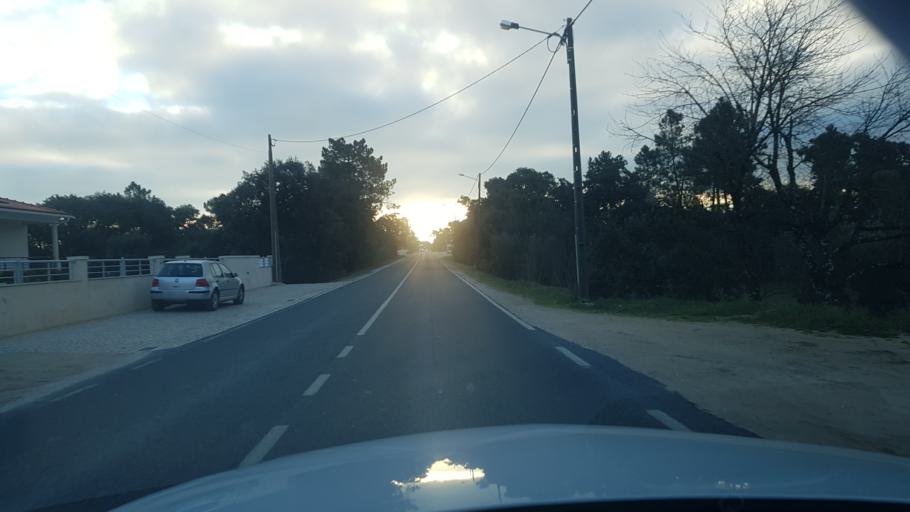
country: PT
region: Santarem
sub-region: Ourem
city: Fatima
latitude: 39.5998
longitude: -8.6482
